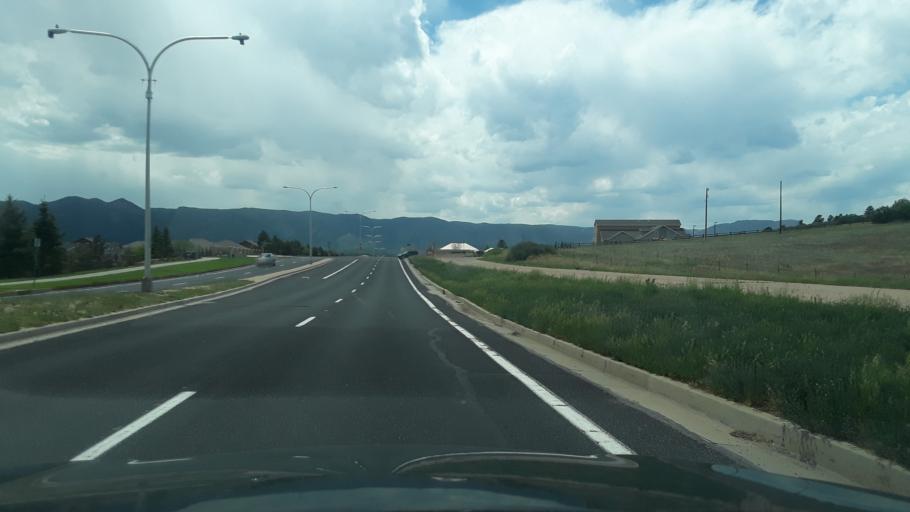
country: US
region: Colorado
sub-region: El Paso County
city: Gleneagle
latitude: 39.0273
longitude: -104.8061
